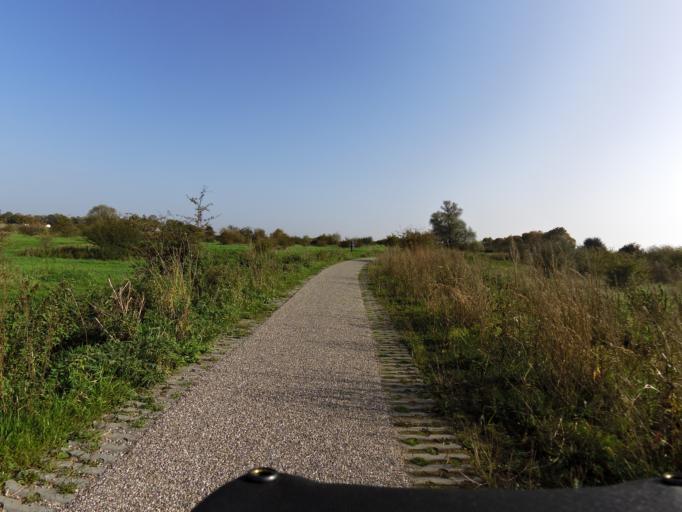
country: NL
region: Gelderland
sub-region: Gemeente Groesbeek
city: Berg en Dal
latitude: 51.8682
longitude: 5.9758
